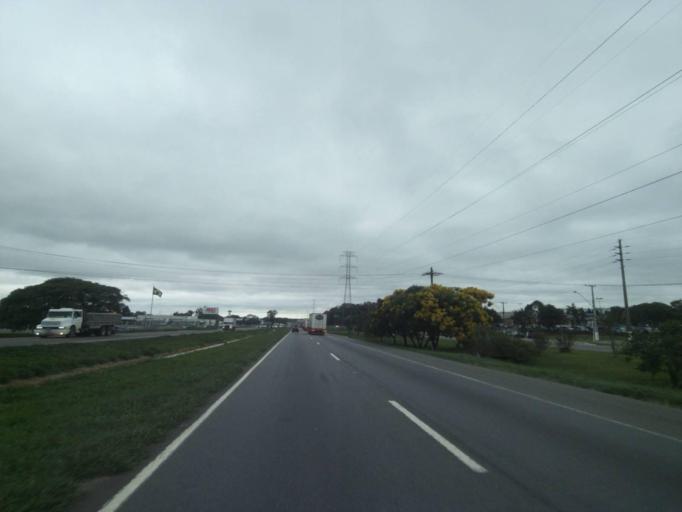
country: BR
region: Parana
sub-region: Curitiba
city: Curitiba
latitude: -25.4536
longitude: -49.3618
